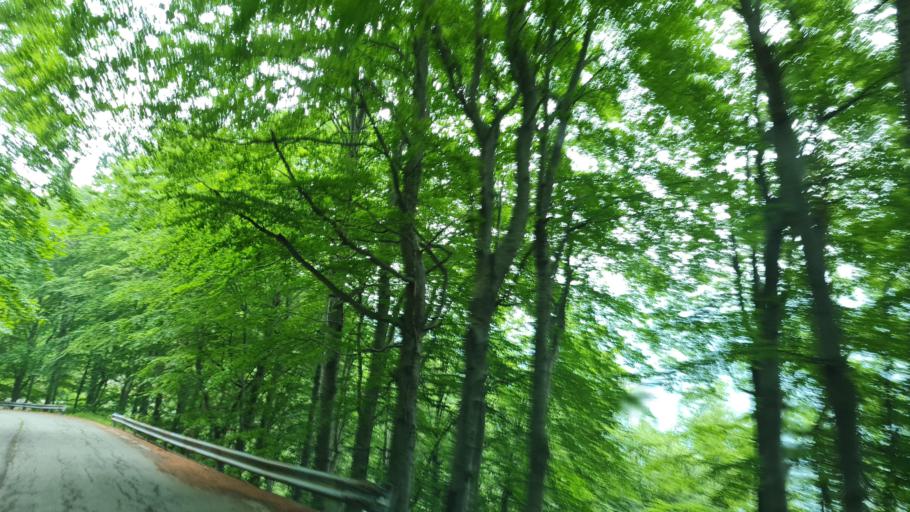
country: IT
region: Piedmont
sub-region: Provincia di Biella
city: Sordevolo
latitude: 45.6163
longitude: 7.9806
